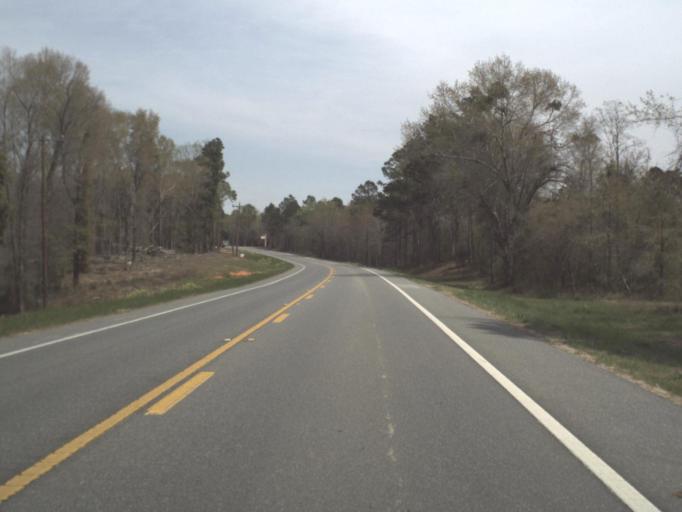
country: US
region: Florida
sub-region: Jackson County
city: Graceville
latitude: 30.9603
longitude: -85.6605
